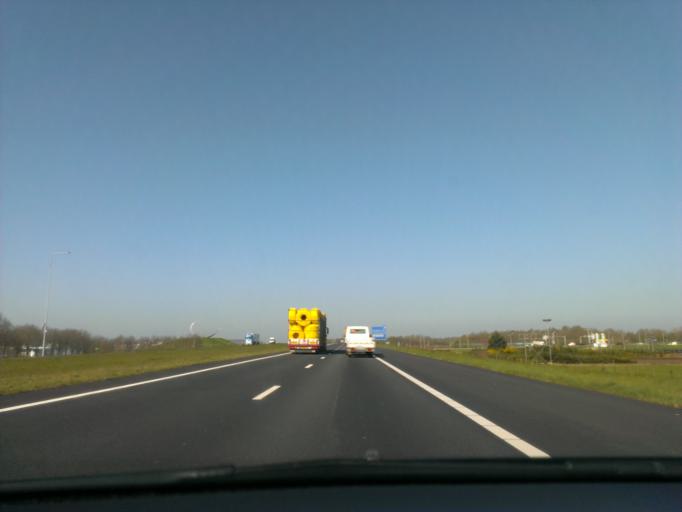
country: NL
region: Drenthe
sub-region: Gemeente Hoogeveen
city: Hoogeveen
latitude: 52.7162
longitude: 6.5229
